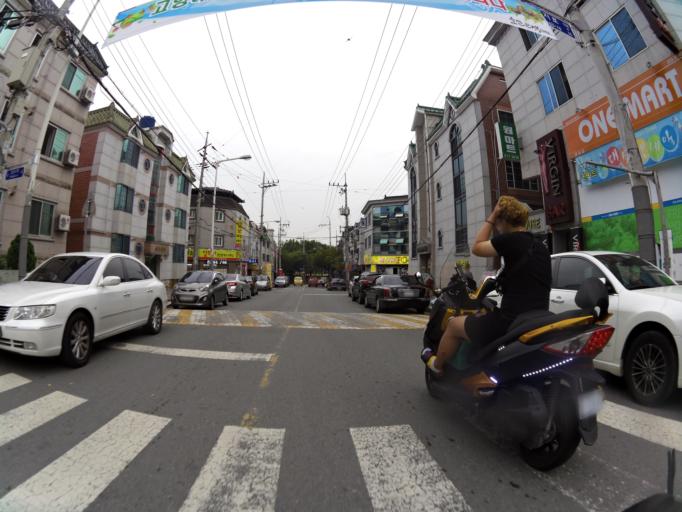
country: KR
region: Gyeongsangbuk-do
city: Gyeongsan-si
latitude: 35.8413
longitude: 128.7536
